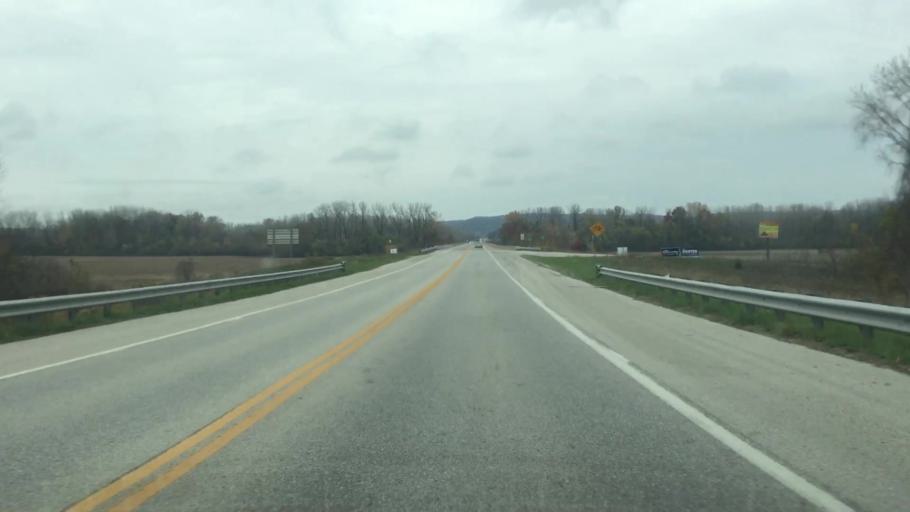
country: US
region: Missouri
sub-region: Gasconade County
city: Hermann
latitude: 38.7134
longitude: -91.4403
